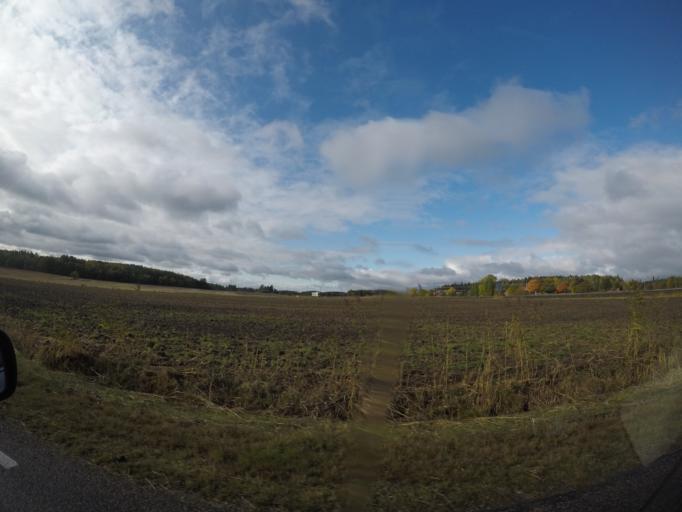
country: SE
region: Soedermanland
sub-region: Eskilstuna Kommun
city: Kvicksund
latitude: 59.4071
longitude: 16.2444
